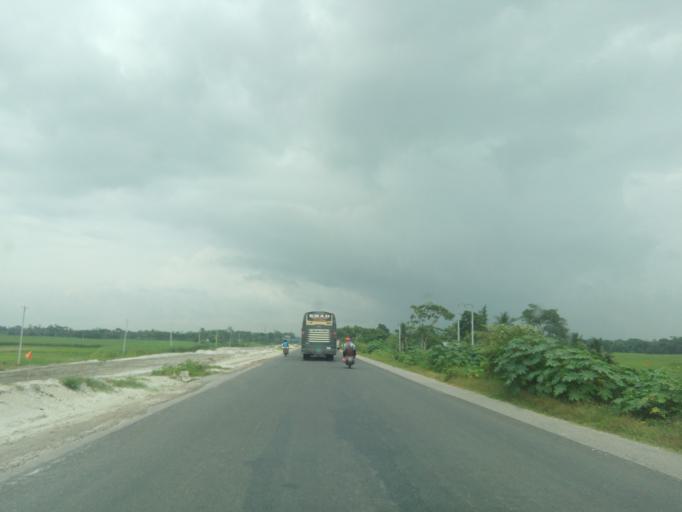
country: BD
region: Dhaka
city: Char Bhadrasan
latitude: 23.3699
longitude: 90.0539
